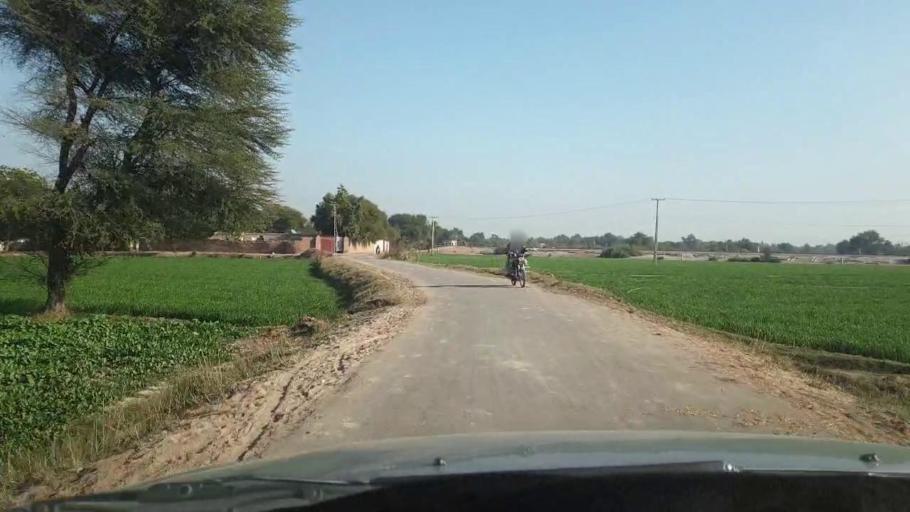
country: PK
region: Sindh
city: Mirpur Mathelo
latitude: 28.0203
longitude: 69.5826
